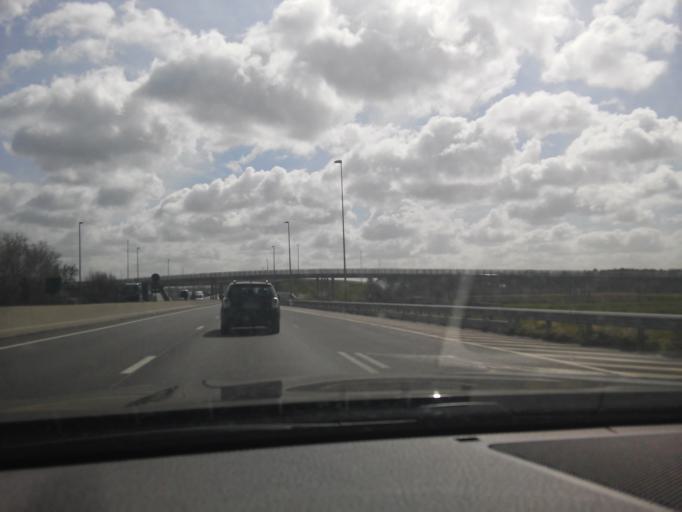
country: BE
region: Flanders
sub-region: Provincie West-Vlaanderen
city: Oostkamp
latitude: 51.1727
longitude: 3.2057
